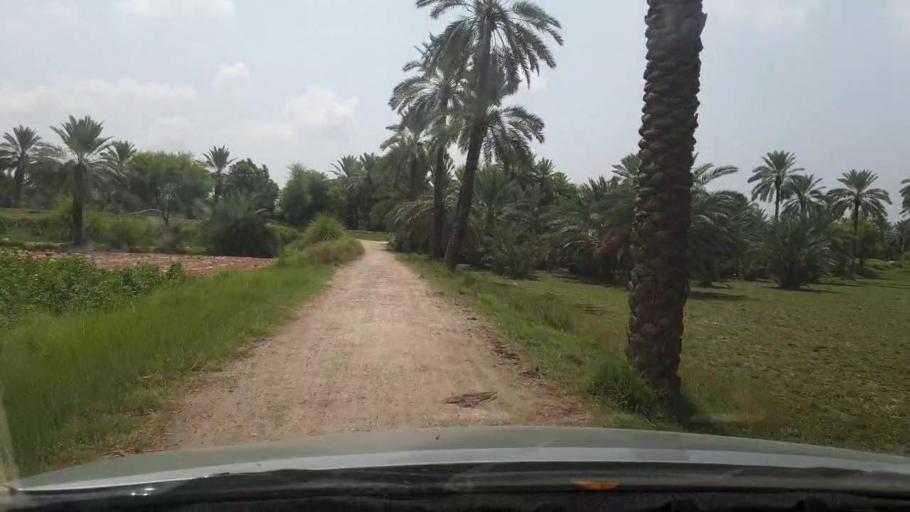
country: PK
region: Sindh
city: Khairpur
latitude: 27.4832
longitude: 68.7337
